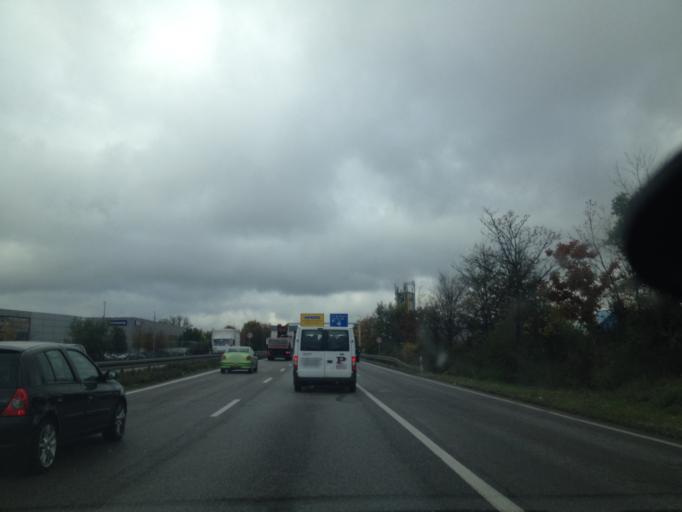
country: DE
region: Bavaria
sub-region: Swabia
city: Gersthofen
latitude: 48.4084
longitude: 10.8746
